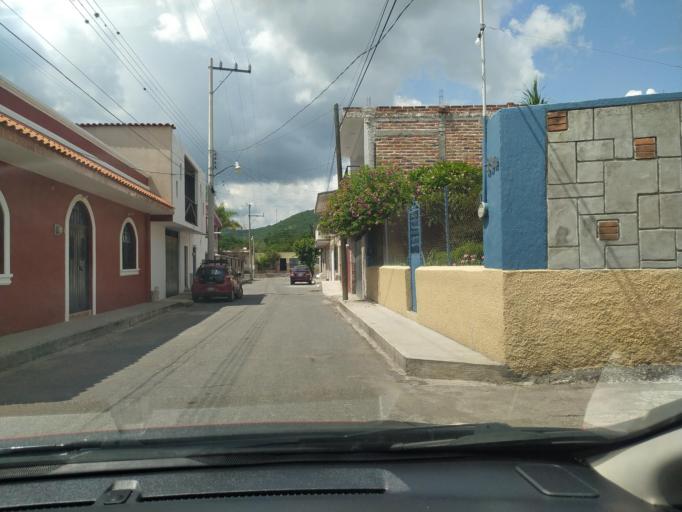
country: MX
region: Jalisco
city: Villa Corona
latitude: 20.3510
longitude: -103.6759
